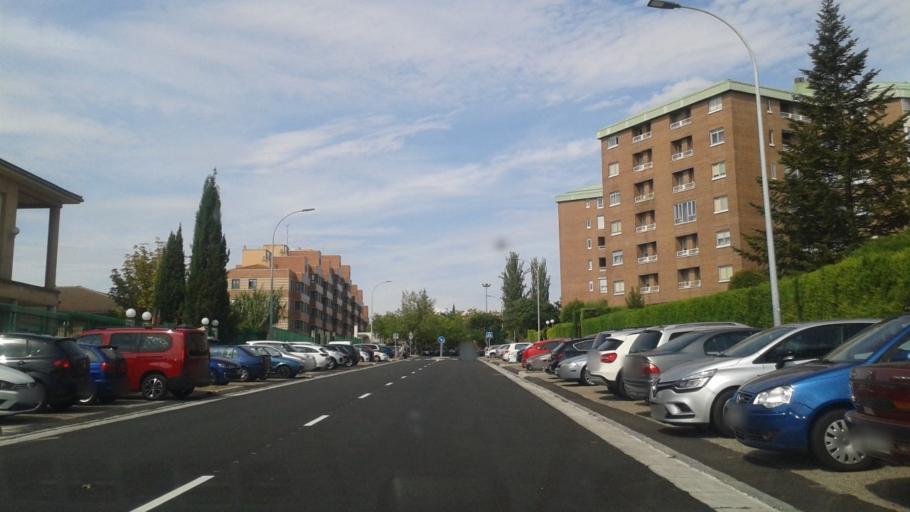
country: ES
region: Castille and Leon
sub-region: Provincia de Valladolid
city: Zaratan
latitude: 41.6326
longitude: -4.7590
